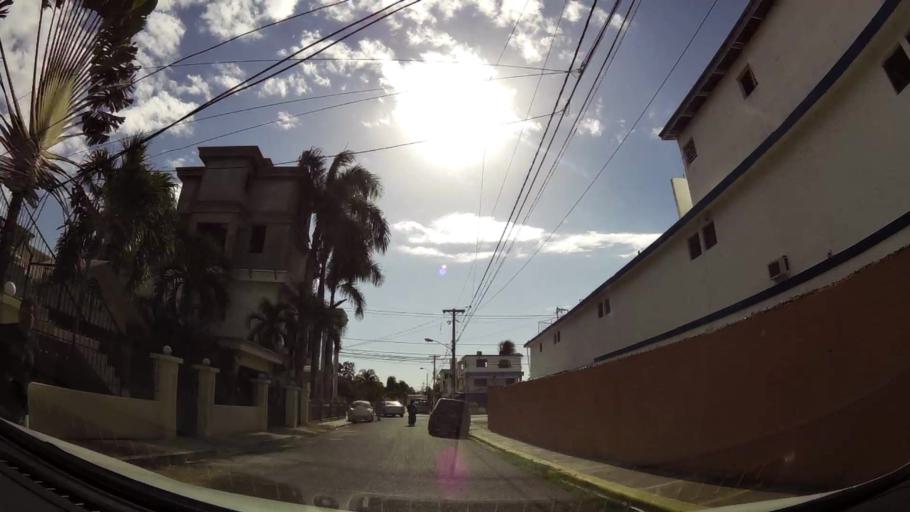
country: DO
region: Santo Domingo
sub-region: Santo Domingo
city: Boca Chica
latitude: 18.4529
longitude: -69.6091
